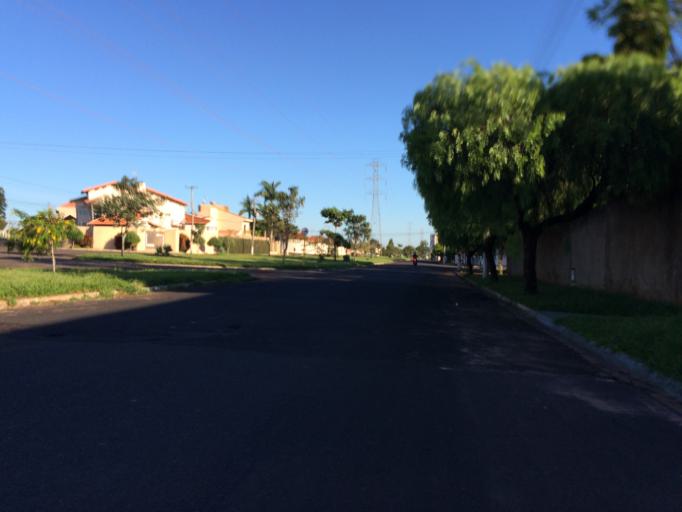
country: BR
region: Sao Paulo
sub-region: Matao
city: Matao
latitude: -21.6216
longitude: -48.3612
